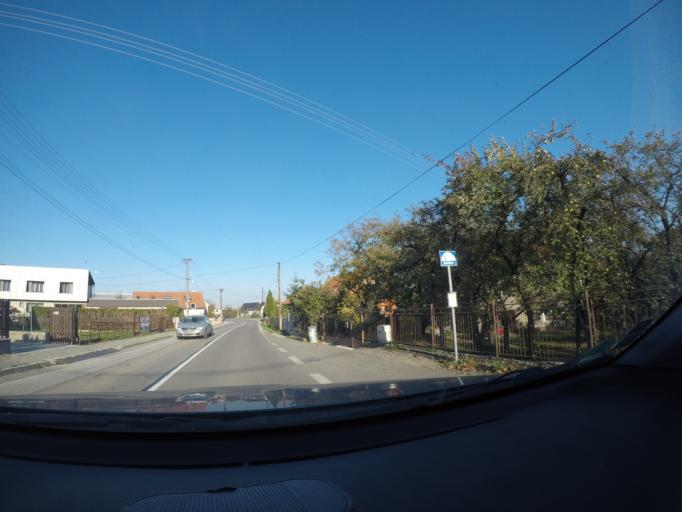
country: SK
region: Trenciansky
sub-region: Okres Trencin
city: Trencin
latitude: 48.9336
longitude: 18.0744
